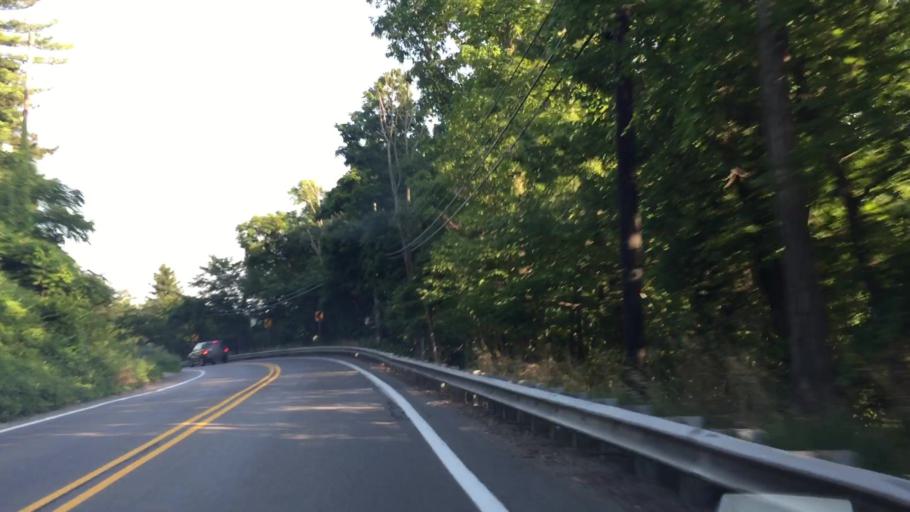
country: US
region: Pennsylvania
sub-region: Washington County
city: Thompsonville
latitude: 40.3220
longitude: -80.1223
